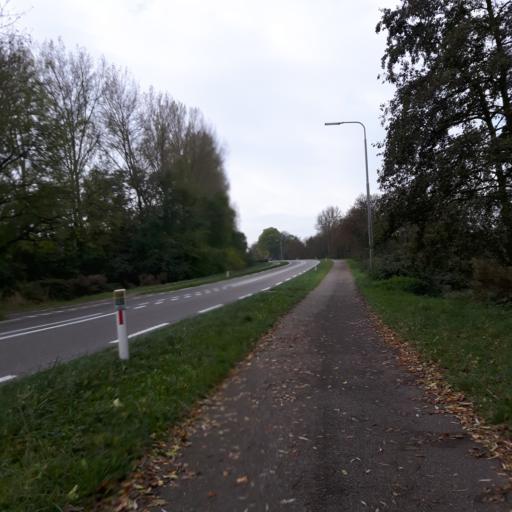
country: NL
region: Zeeland
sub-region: Gemeente Goes
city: Goes
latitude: 51.5007
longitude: 3.8383
